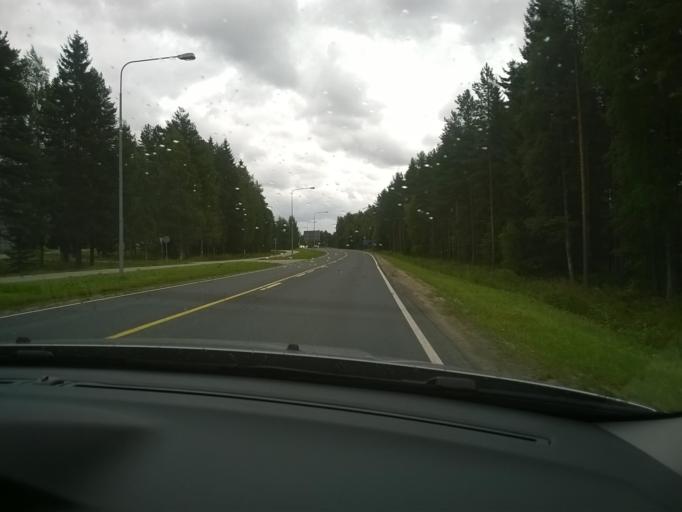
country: FI
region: Kainuu
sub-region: Kehys-Kainuu
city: Kuhmo
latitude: 64.1218
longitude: 29.5103
